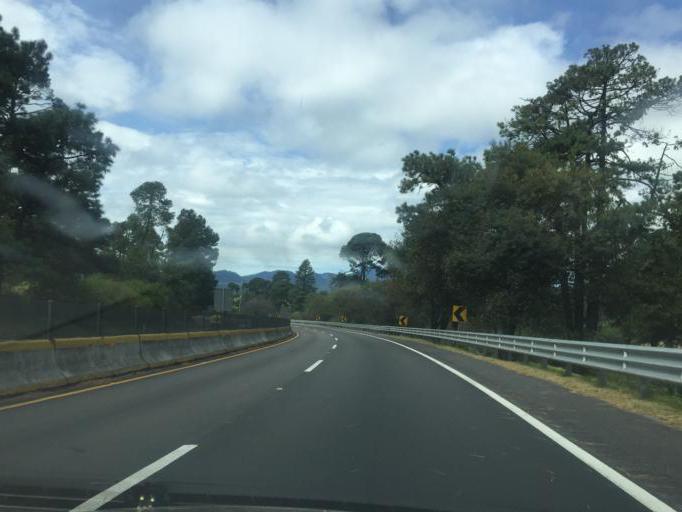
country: MX
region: Morelos
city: Tres Marias
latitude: 19.0837
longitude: -99.2296
